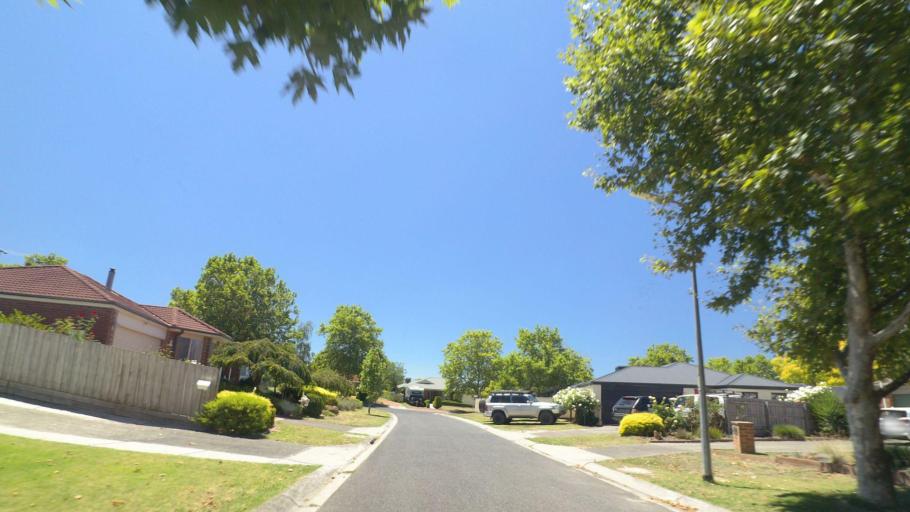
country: AU
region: Victoria
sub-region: Yarra Ranges
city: Lilydale
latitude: -37.7422
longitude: 145.3452
